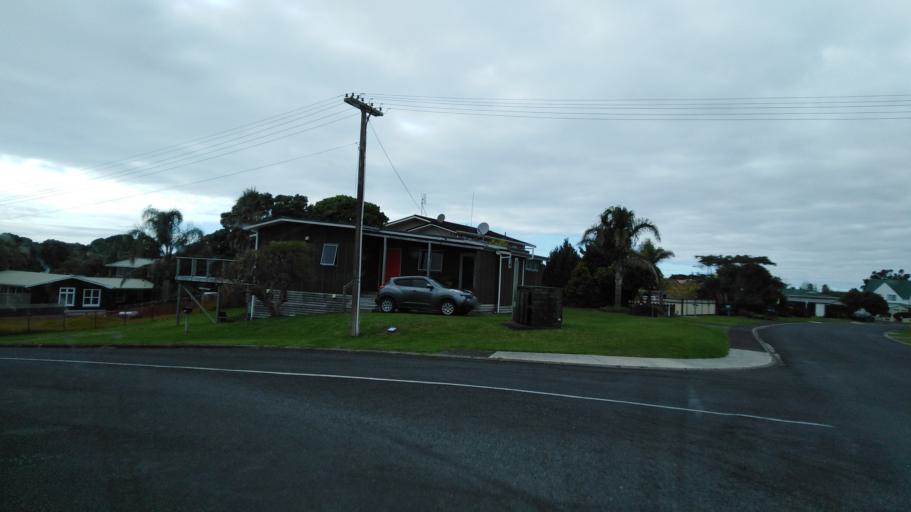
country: NZ
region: Bay of Plenty
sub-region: Western Bay of Plenty District
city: Waihi Beach
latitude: -37.4136
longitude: 175.9428
